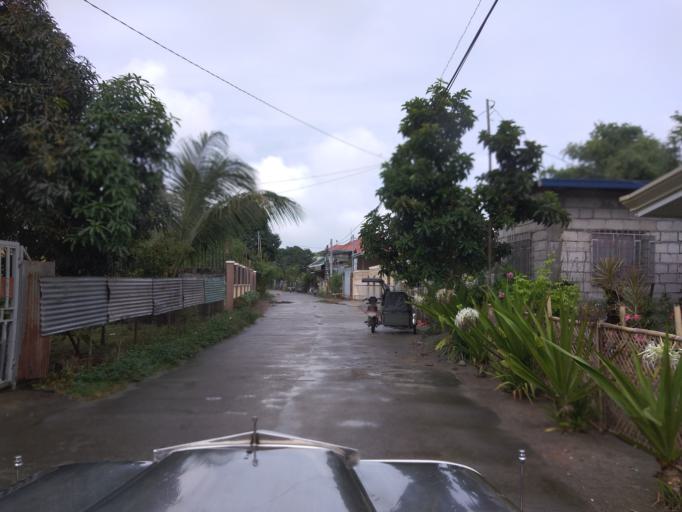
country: PH
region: Central Luzon
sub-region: Province of Pampanga
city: Santo Domingo
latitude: 15.0714
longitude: 120.7602
